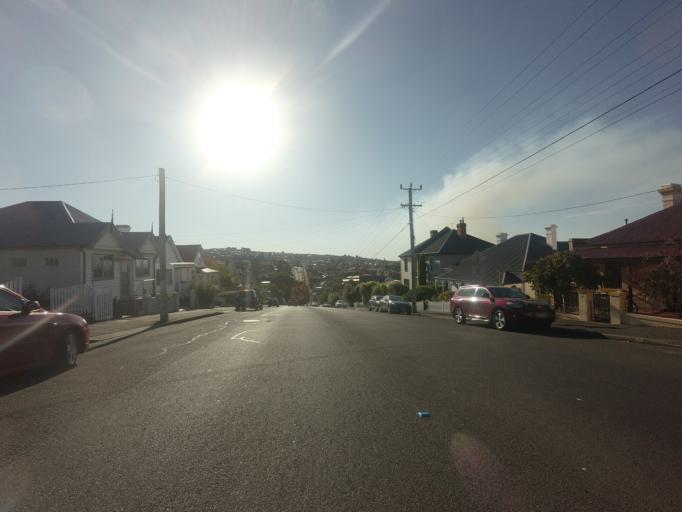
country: AU
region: Tasmania
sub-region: Hobart
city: Sandy Bay
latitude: -42.8833
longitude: 147.3145
